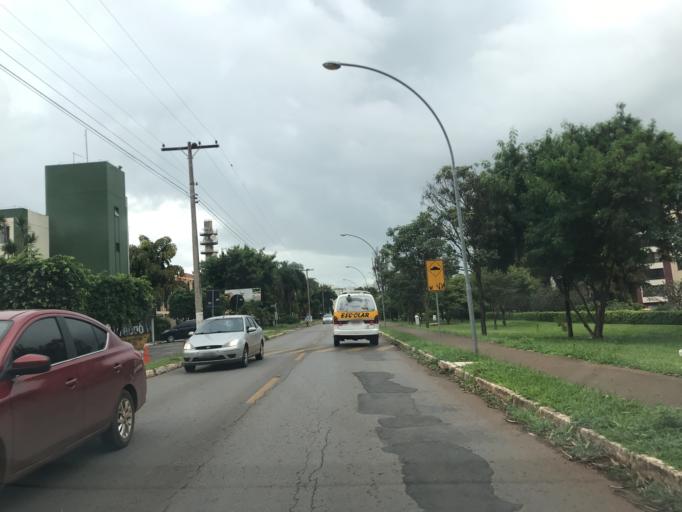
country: BR
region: Federal District
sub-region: Brasilia
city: Brasilia
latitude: -15.7954
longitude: -47.9228
